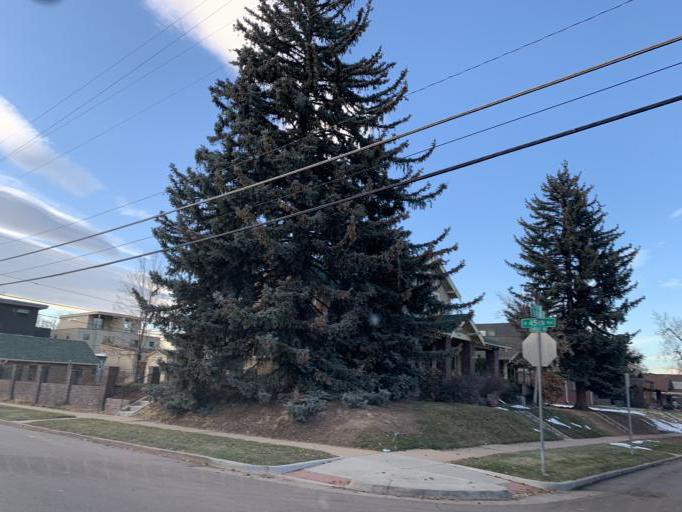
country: US
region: Colorado
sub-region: Jefferson County
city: Edgewater
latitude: 39.7785
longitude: -105.0452
